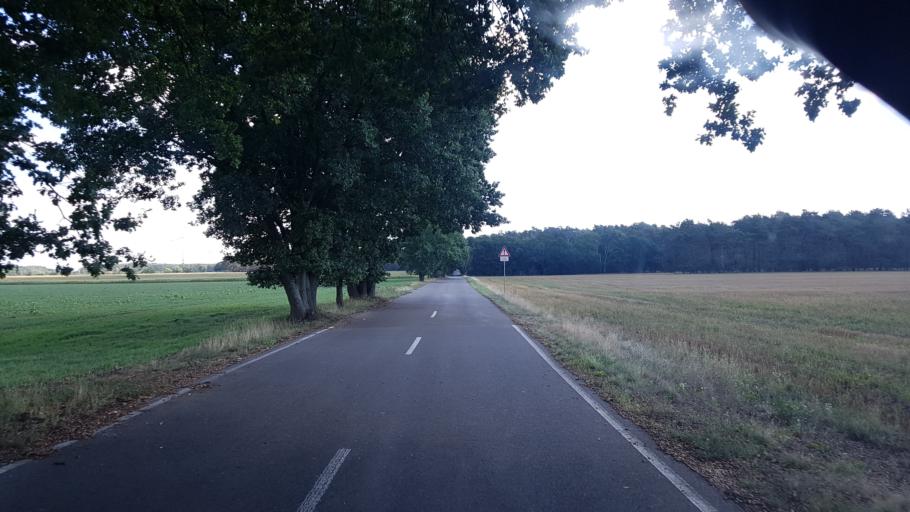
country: DE
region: Brandenburg
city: Drebkau
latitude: 51.6532
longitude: 14.2459
